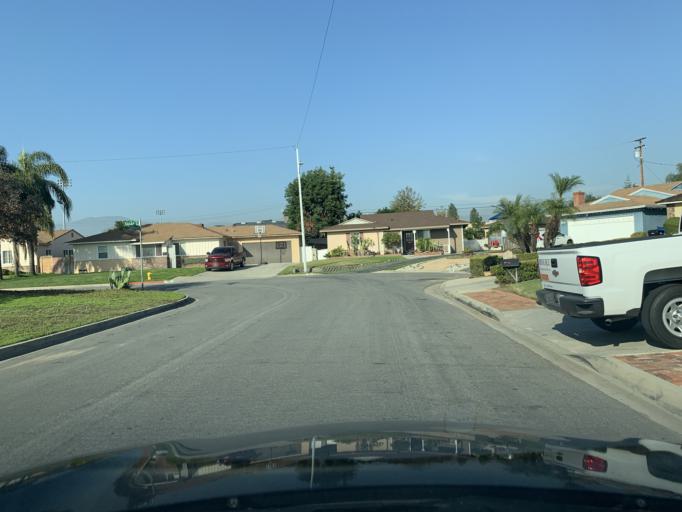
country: US
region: California
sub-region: Los Angeles County
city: Covina
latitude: 34.0802
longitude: -117.8918
